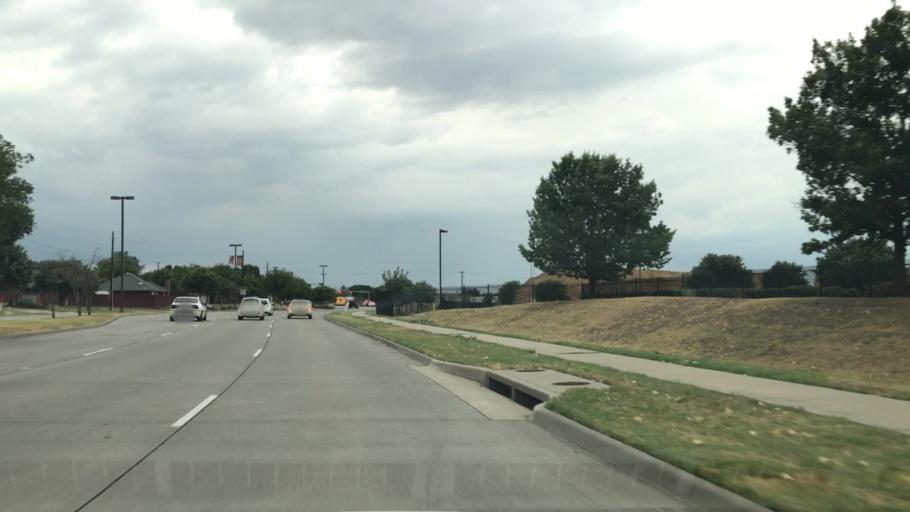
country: US
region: Texas
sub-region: Dallas County
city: Carrollton
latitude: 32.9712
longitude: -96.9116
